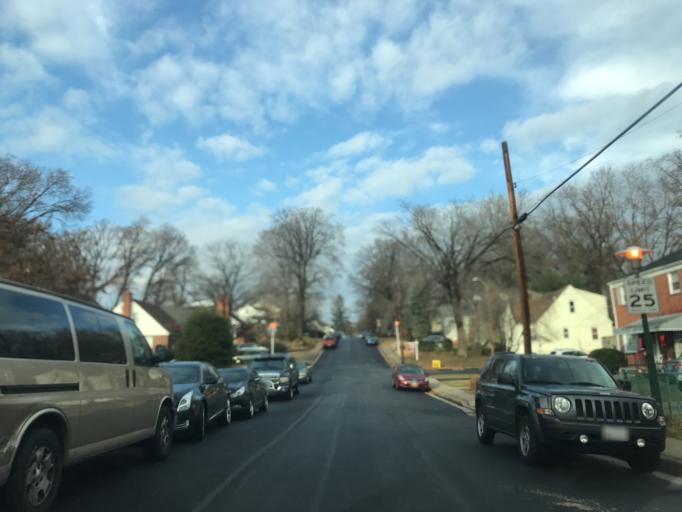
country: US
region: Maryland
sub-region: Baltimore County
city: Overlea
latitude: 39.3542
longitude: -76.5402
